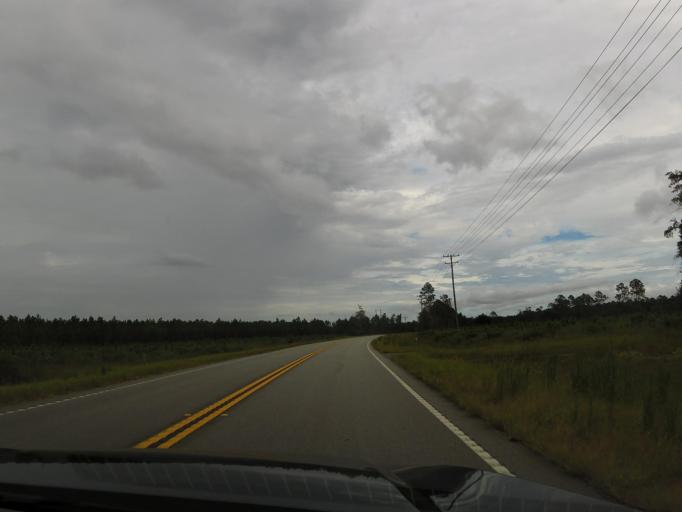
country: US
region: Florida
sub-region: Nassau County
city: Hilliard
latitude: 30.5220
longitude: -82.0829
